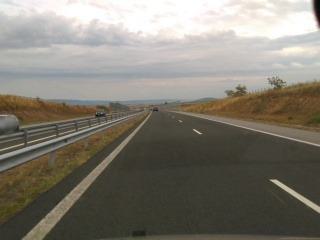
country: BG
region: Sliven
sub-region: Obshtina Sliven
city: Kermen
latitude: 42.5150
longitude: 26.3715
